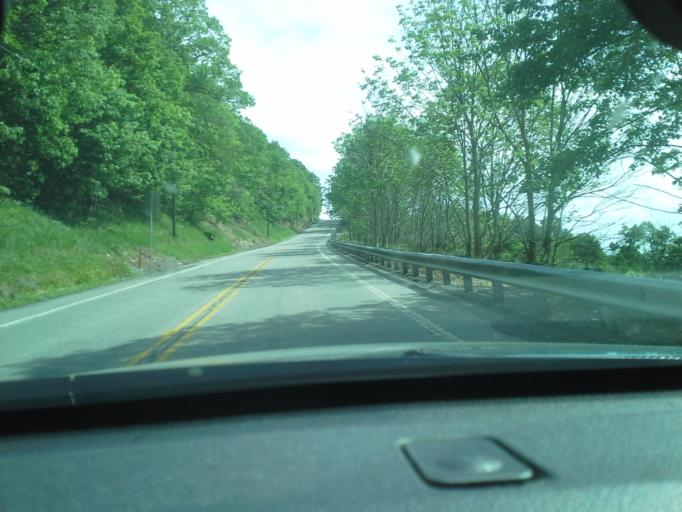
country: US
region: Pennsylvania
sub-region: Fulton County
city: McConnellsburg
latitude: 39.9044
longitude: -77.9666
